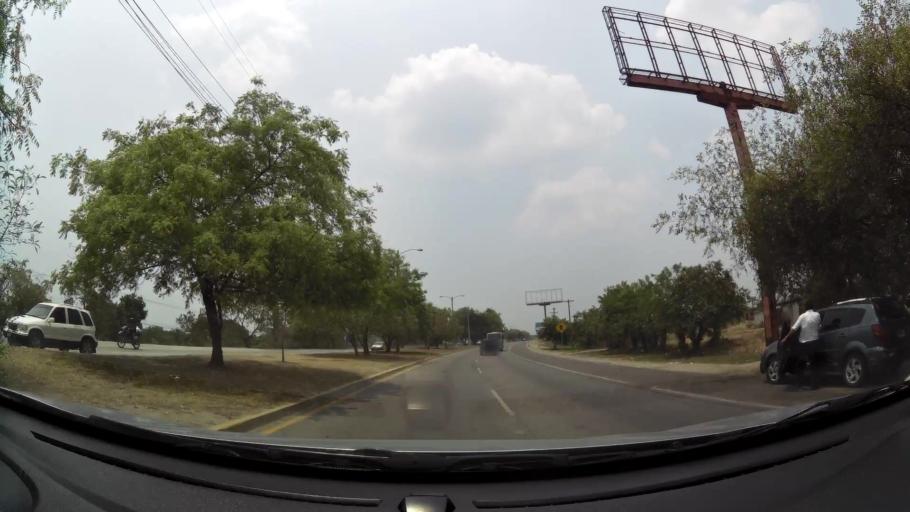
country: HN
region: Cortes
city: La Lima
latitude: 15.4525
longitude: -87.9469
